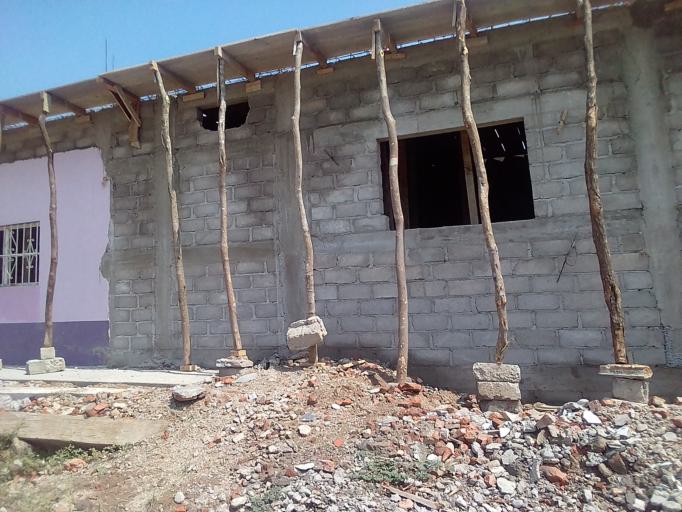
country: MX
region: Oaxaca
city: Union Hidalgo
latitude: 16.4699
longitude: -94.8310
